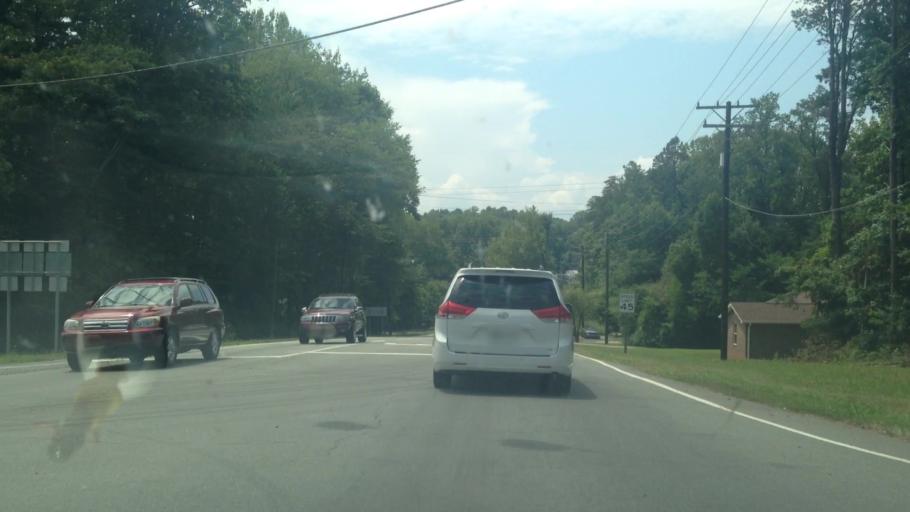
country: US
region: North Carolina
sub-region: Forsyth County
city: Walkertown
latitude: 36.1705
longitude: -80.1608
